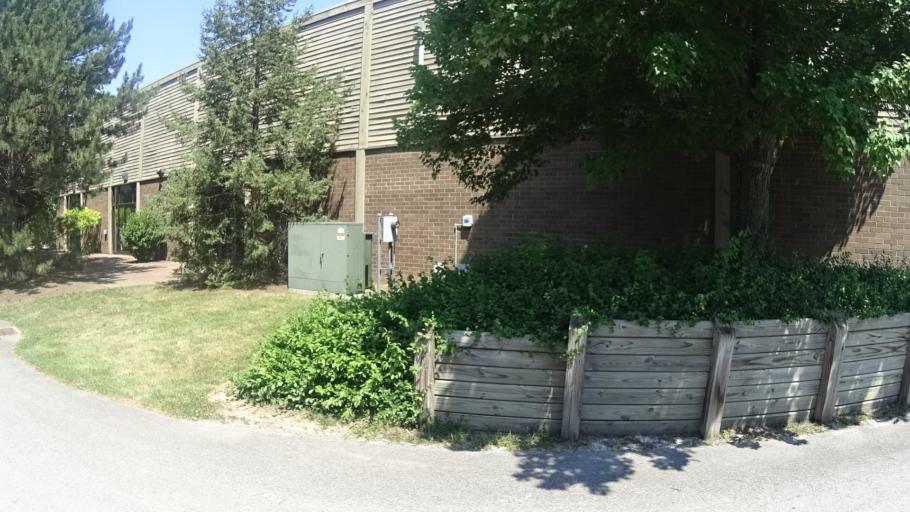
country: US
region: Ohio
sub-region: Erie County
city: Huron
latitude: 41.4077
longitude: -82.5959
